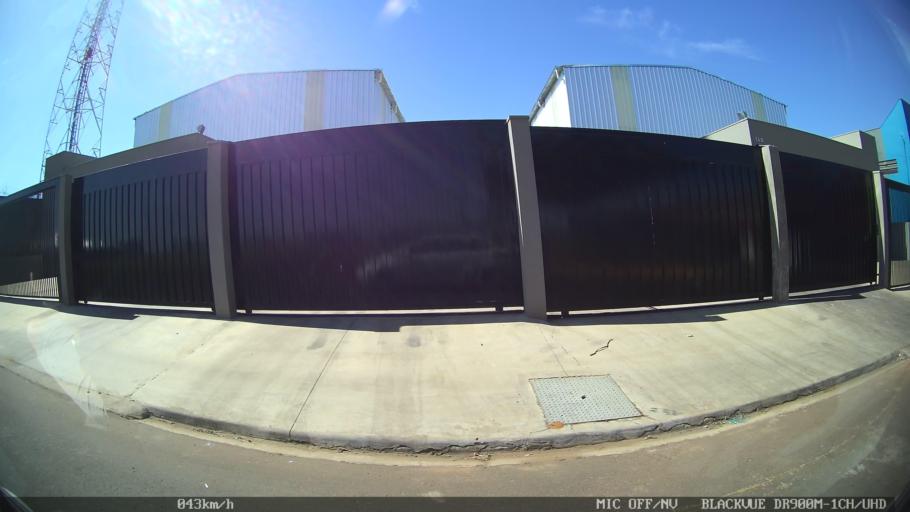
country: BR
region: Sao Paulo
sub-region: Franca
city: Franca
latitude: -20.5436
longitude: -47.4642
